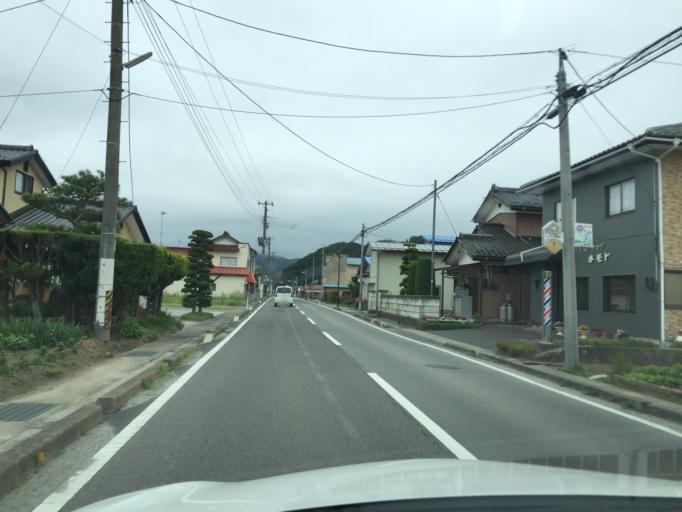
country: JP
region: Fukushima
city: Funehikimachi-funehiki
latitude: 37.3511
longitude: 140.6452
